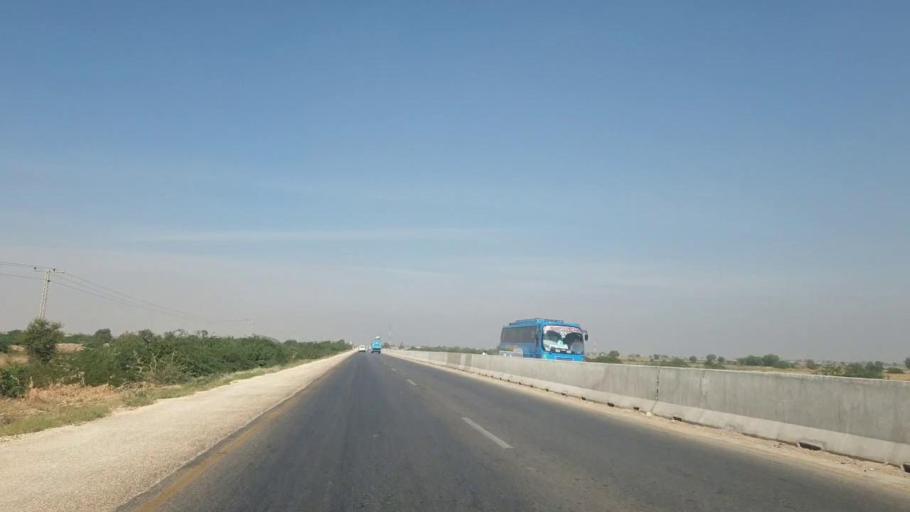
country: PK
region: Sindh
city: Matiari
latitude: 25.6365
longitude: 68.3016
